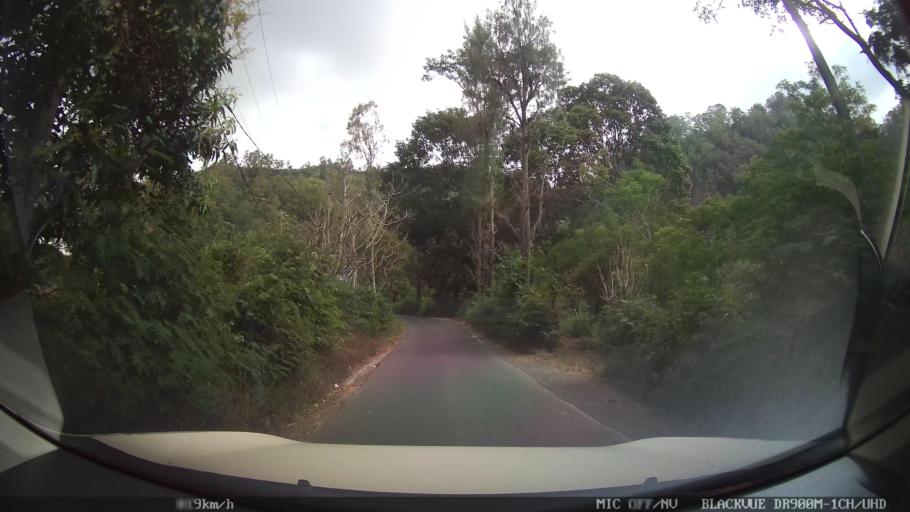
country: ID
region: Bali
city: Banjar Kedisan
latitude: -8.2476
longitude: 115.3482
